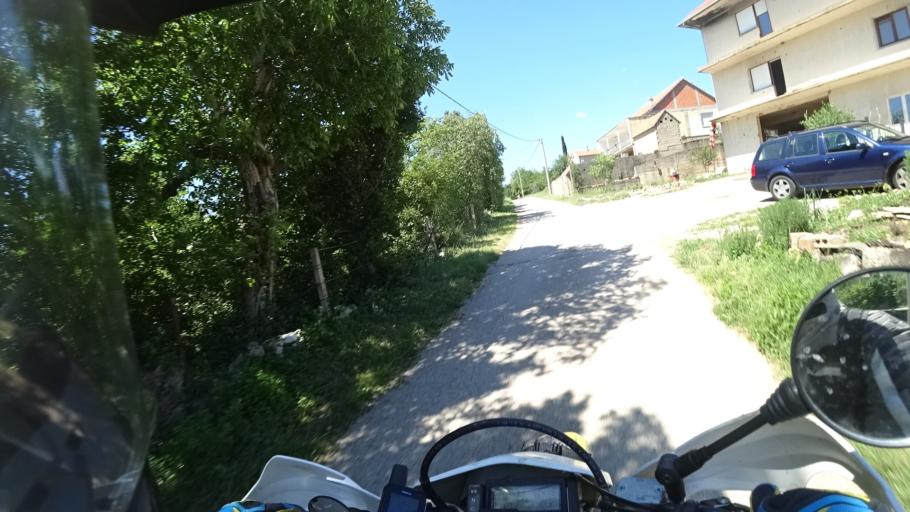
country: BA
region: Federation of Bosnia and Herzegovina
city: Bosansko Grahovo
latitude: 43.9779
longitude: 16.4278
